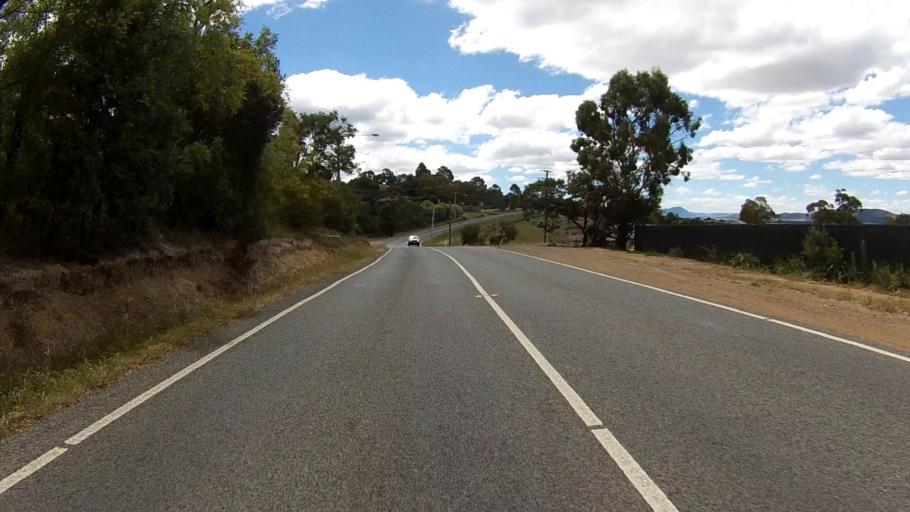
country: AU
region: Tasmania
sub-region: Clarence
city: Acton Park
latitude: -42.8599
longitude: 147.4763
